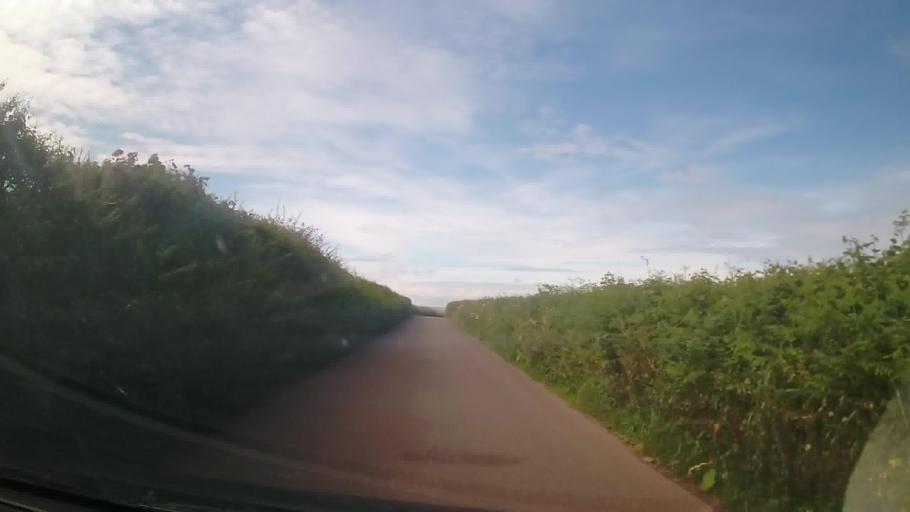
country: GB
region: England
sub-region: Devon
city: Salcombe
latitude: 50.2472
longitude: -3.6819
